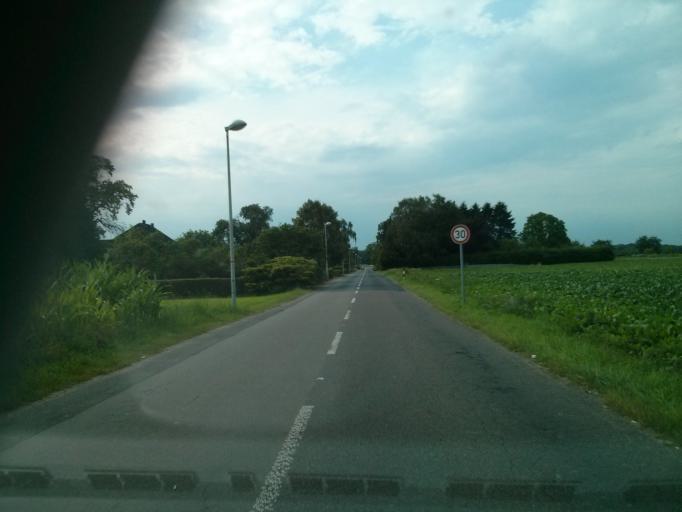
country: DE
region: North Rhine-Westphalia
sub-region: Regierungsbezirk Dusseldorf
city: Krefeld
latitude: 51.3857
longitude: 6.5553
